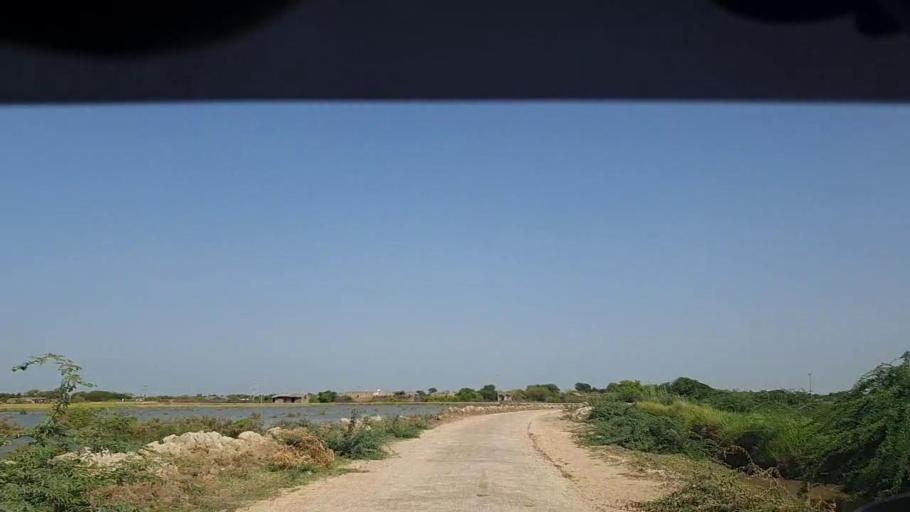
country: PK
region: Sindh
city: Badin
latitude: 24.4581
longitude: 68.7637
